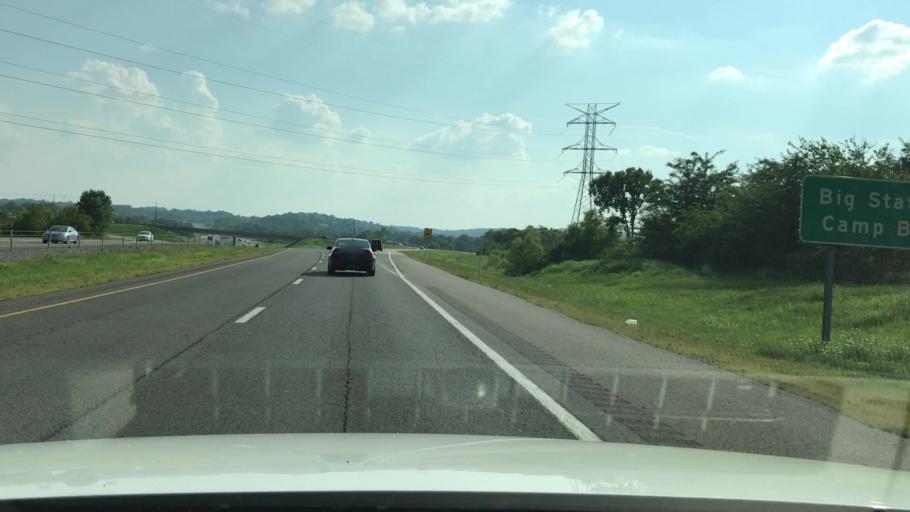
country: US
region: Tennessee
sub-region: Sumner County
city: Gallatin
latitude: 36.3613
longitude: -86.5293
